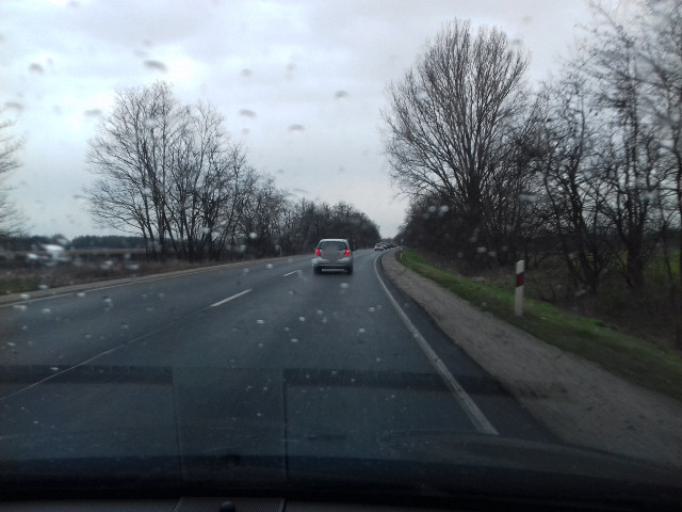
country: HU
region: Szabolcs-Szatmar-Bereg
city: Ujfeherto
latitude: 47.8374
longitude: 21.7043
